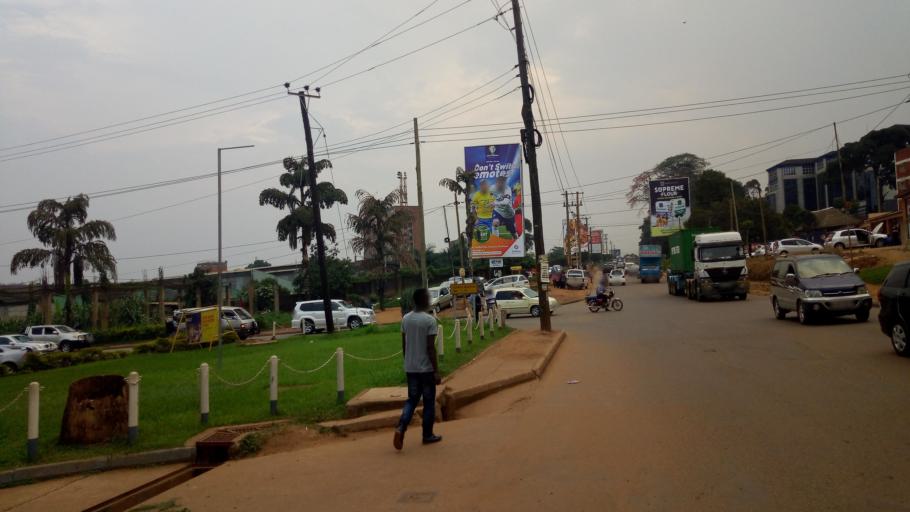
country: UG
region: Central Region
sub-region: Kampala District
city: Kampala
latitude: 0.3206
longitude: 32.6173
